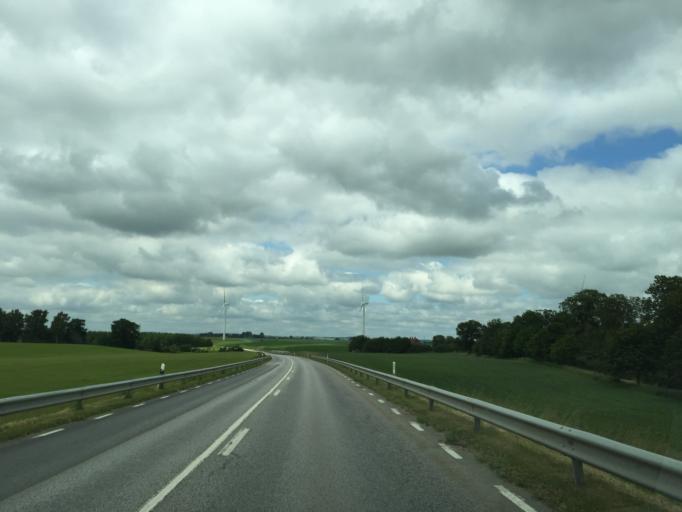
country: SE
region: Skane
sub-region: Svedala Kommun
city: Klagerup
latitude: 55.6019
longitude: 13.2647
